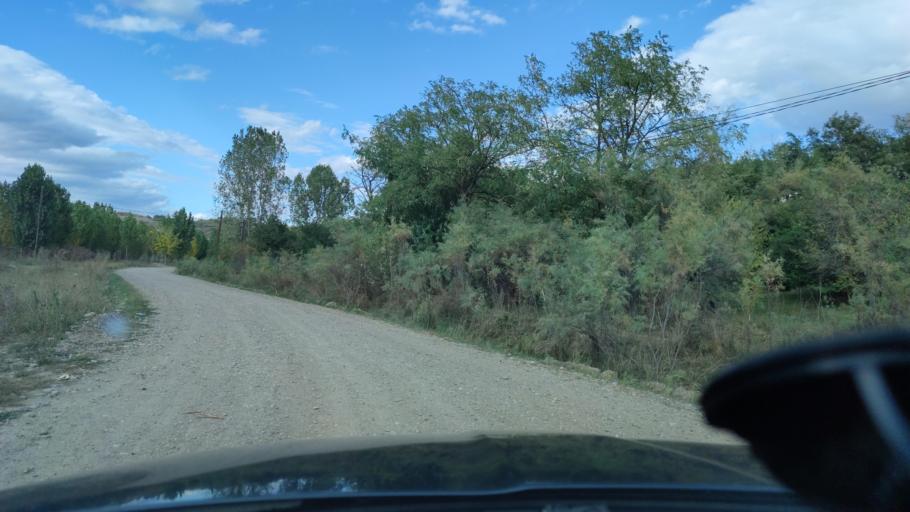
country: RO
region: Buzau
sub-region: Comuna Beceni
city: Valea Parului
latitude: 45.3602
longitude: 26.7706
